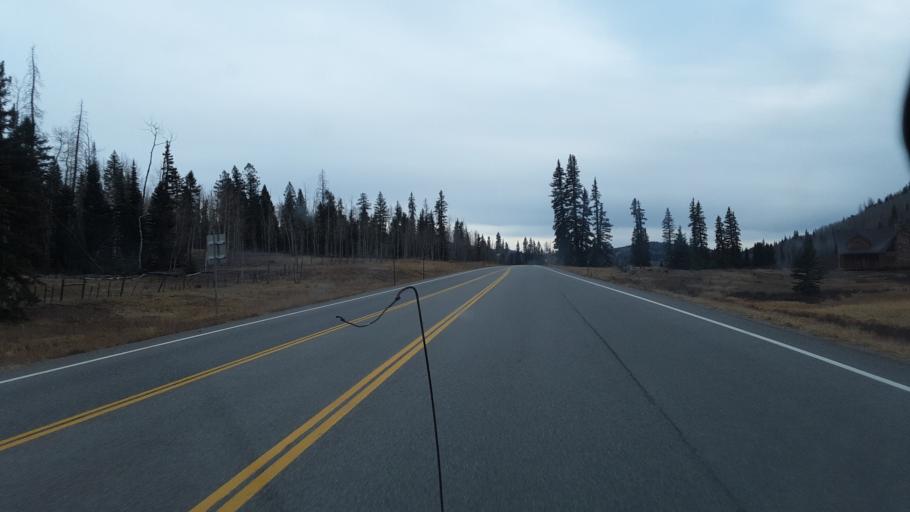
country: US
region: Colorado
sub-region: San Juan County
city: Silverton
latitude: 37.6518
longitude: -107.8092
